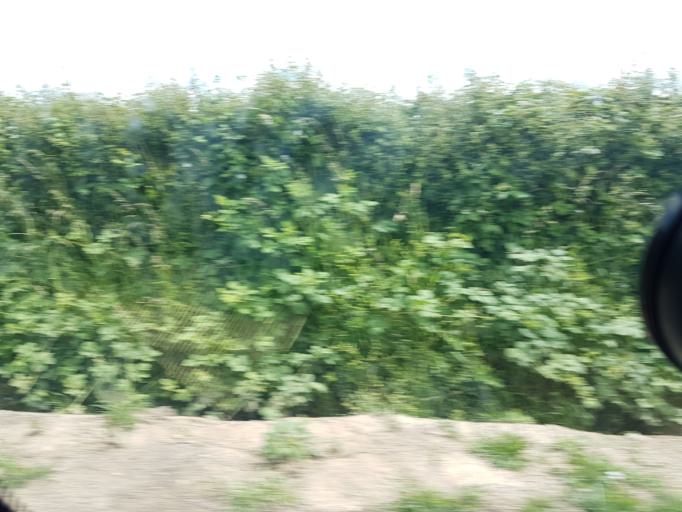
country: FR
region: Bourgogne
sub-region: Departement de Saone-et-Loire
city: Epinac
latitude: 46.9802
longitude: 4.4892
